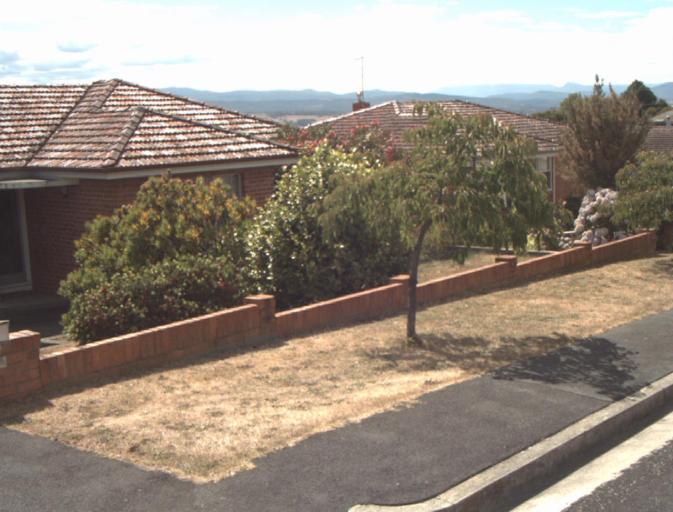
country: AU
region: Tasmania
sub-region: Launceston
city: West Launceston
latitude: -41.4529
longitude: 147.1236
